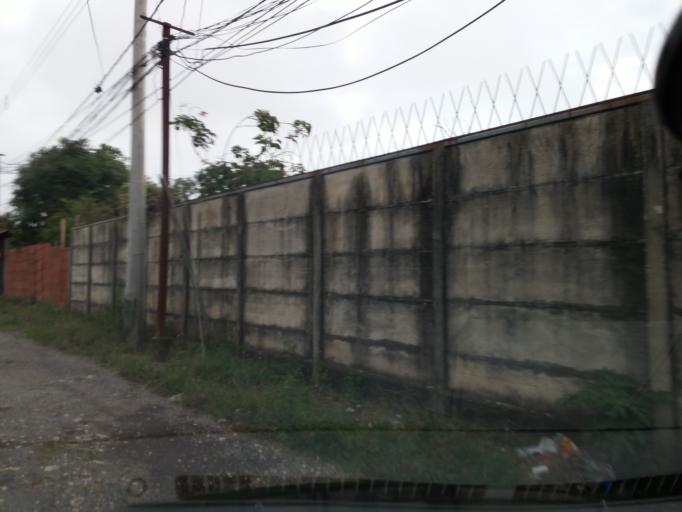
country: CR
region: Heredia
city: San Rafael
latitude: 10.0144
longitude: -84.1081
